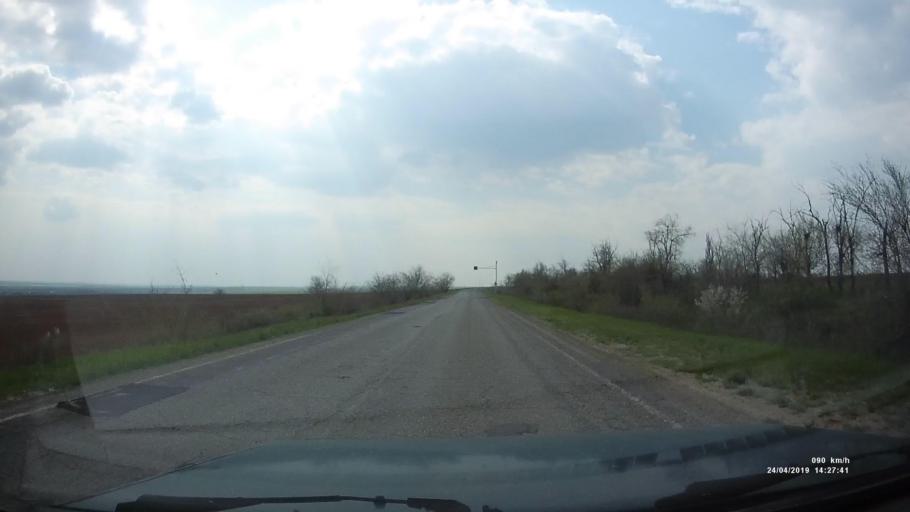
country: RU
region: Kalmykiya
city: Arshan'
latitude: 46.3339
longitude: 44.0385
